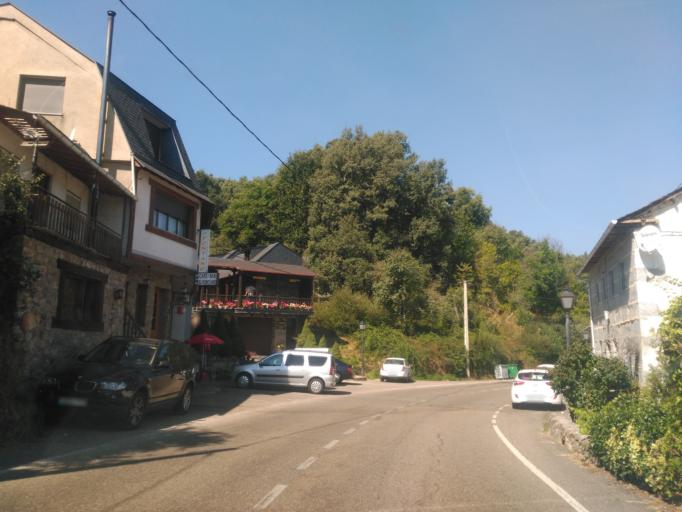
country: ES
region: Castille and Leon
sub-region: Provincia de Zamora
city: Galende
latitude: 42.1047
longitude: -6.6639
